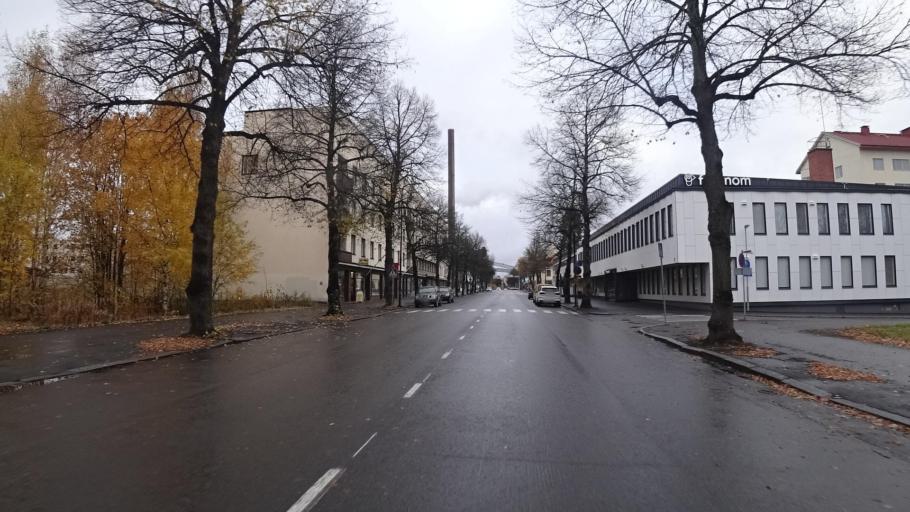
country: FI
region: Northern Savo
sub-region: Varkaus
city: Varkaus
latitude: 62.3134
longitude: 27.8907
